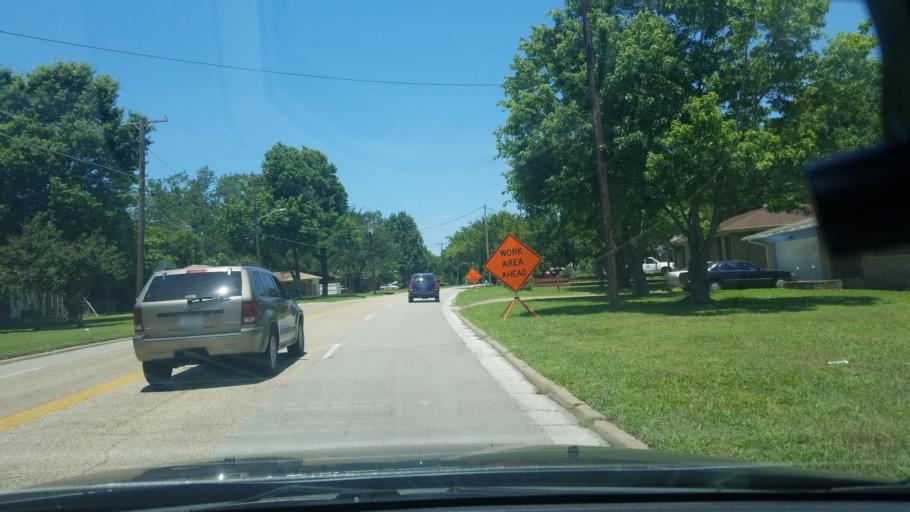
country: US
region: Texas
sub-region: Dallas County
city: Mesquite
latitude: 32.7587
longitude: -96.5986
